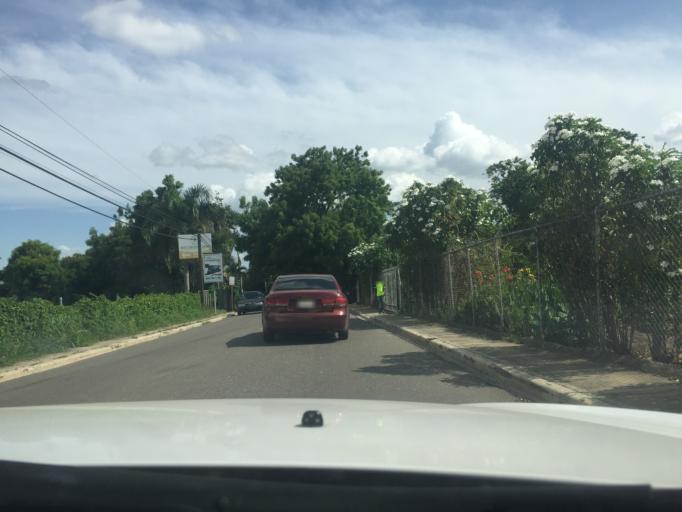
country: DO
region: Santiago
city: Tamboril
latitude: 19.4805
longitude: -70.6558
